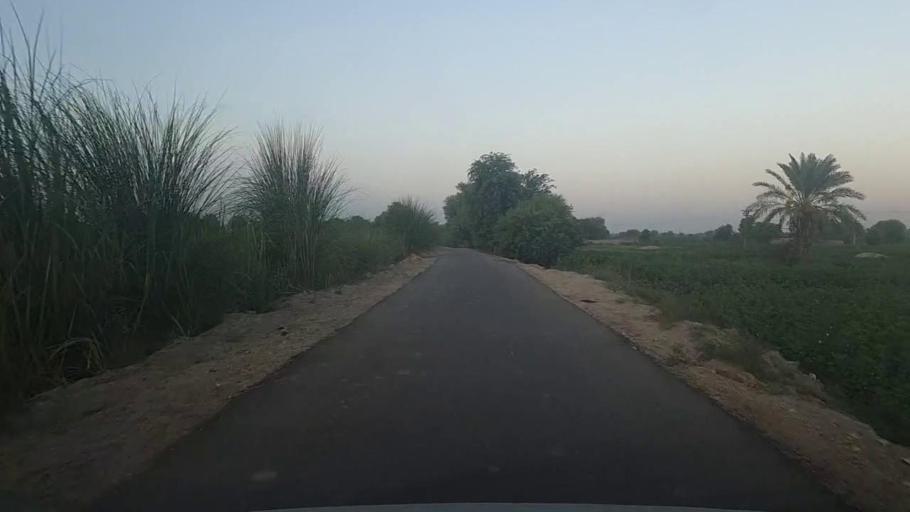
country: PK
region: Sindh
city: Khairpur
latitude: 28.0940
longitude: 69.7343
